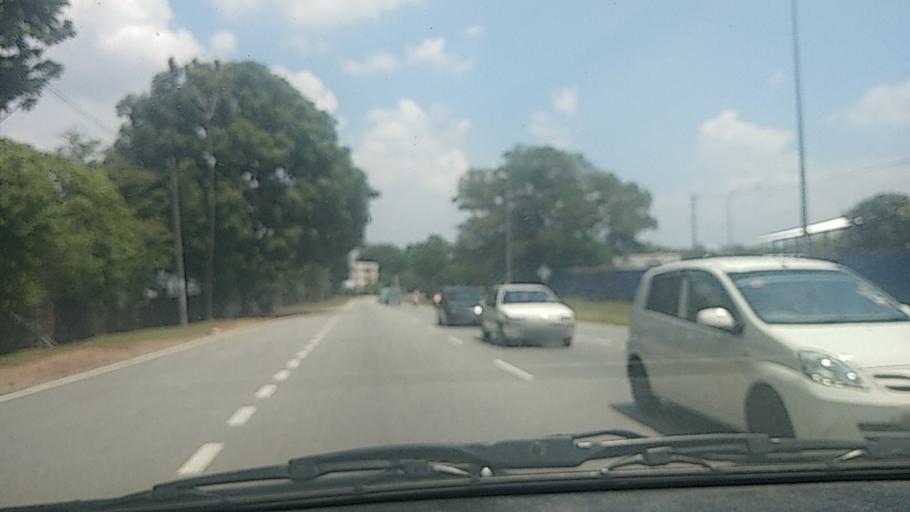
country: MY
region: Kedah
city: Sungai Petani
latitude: 5.6463
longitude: 100.5353
